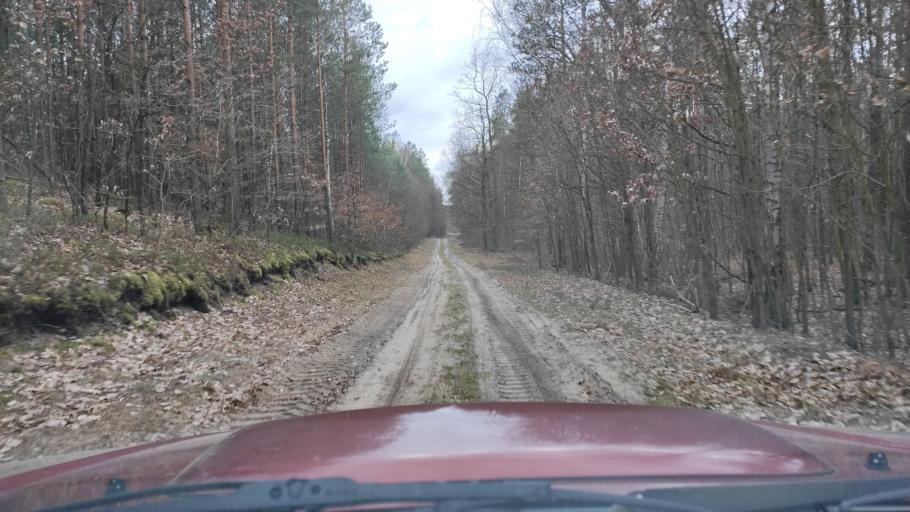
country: PL
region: Masovian Voivodeship
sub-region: Powiat kozienicki
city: Garbatka-Letnisko
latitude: 51.5090
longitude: 21.5488
